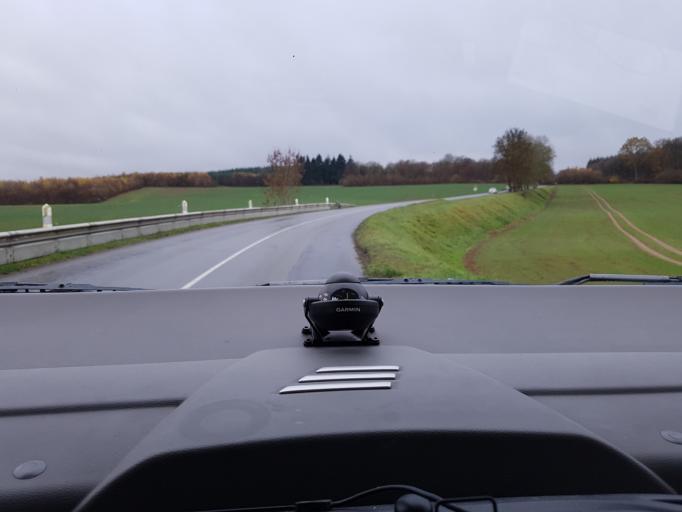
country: FR
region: Haute-Normandie
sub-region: Departement de l'Eure
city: Pont-Saint-Pierre
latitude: 49.3321
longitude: 1.2980
